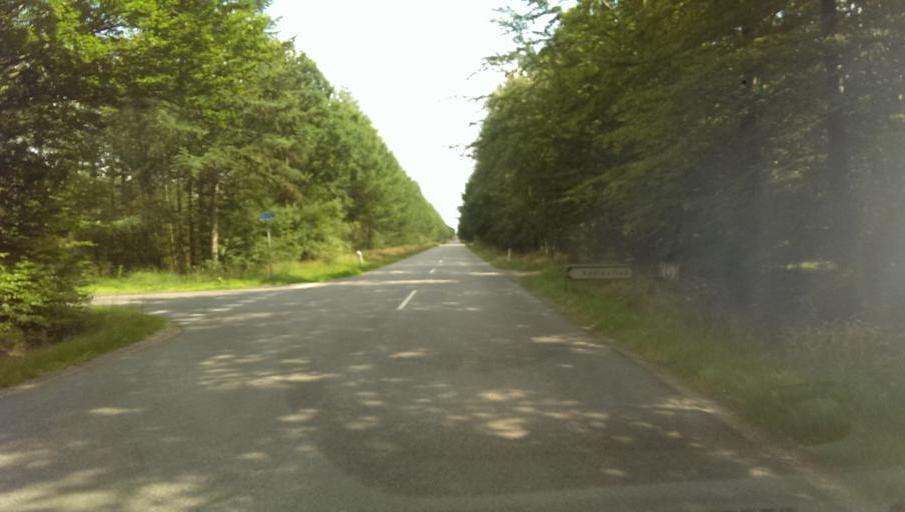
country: DK
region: South Denmark
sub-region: Varde Kommune
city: Varde
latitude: 55.5918
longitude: 8.5379
